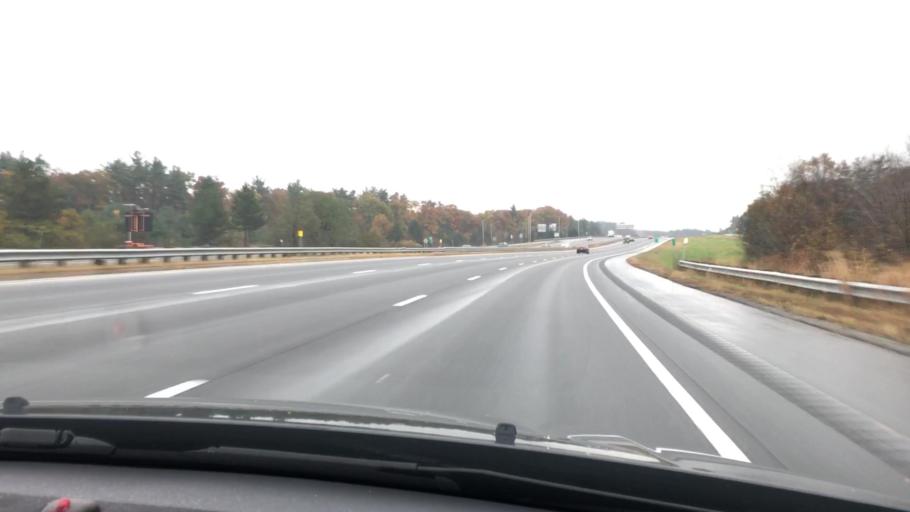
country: US
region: New Hampshire
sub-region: Hillsborough County
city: Hudson
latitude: 42.7195
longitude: -71.4496
